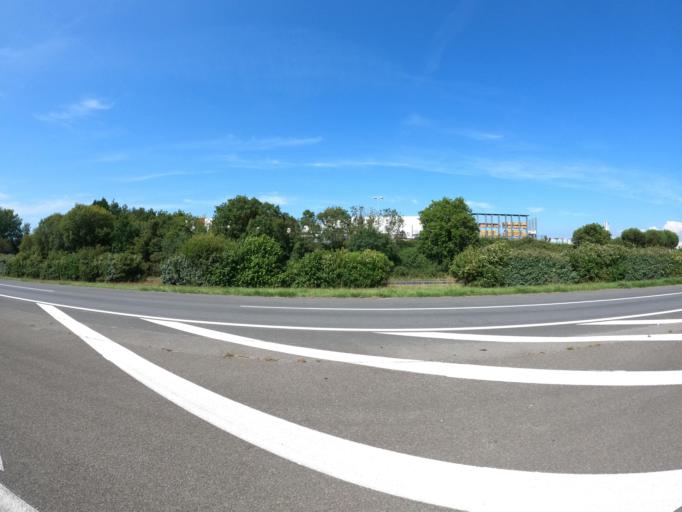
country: FR
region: Pays de la Loire
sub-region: Departement de la Loire-Atlantique
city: Pornic
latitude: 47.1101
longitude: -2.0723
